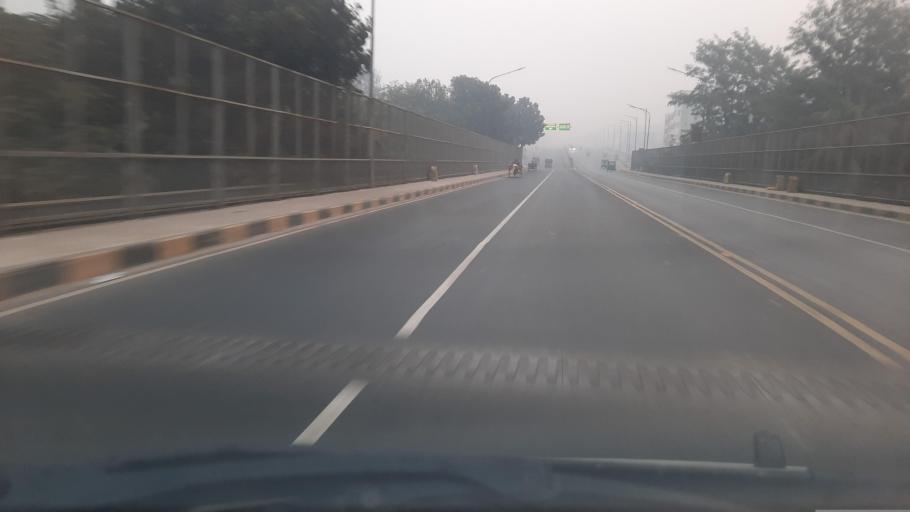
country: BD
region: Dhaka
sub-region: Dhaka
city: Dhaka
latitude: 23.6885
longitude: 90.4285
